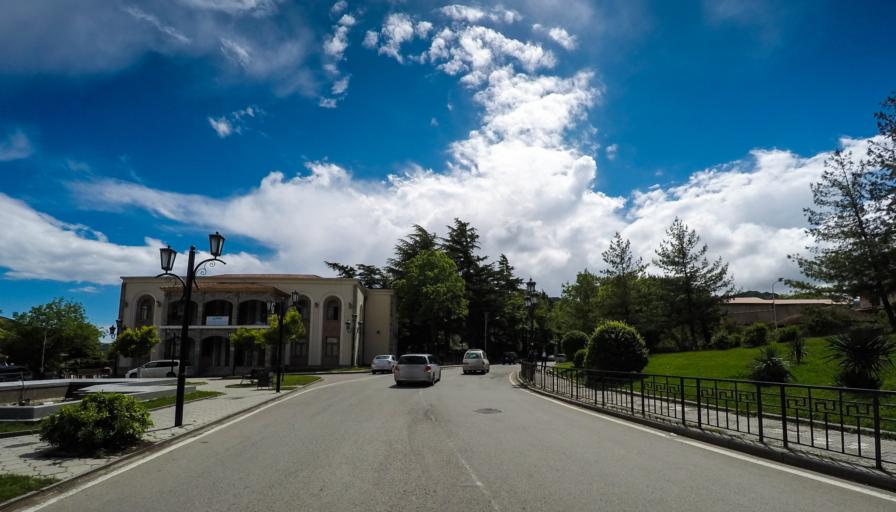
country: GE
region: Mtskheta-Mtianeti
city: Mtskheta
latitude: 41.8453
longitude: 44.7203
